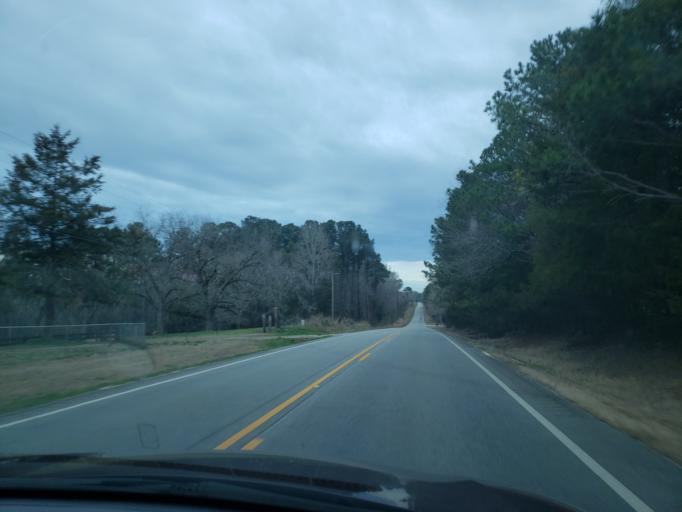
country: US
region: Alabama
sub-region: Chambers County
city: Lafayette
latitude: 32.9691
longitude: -85.4033
